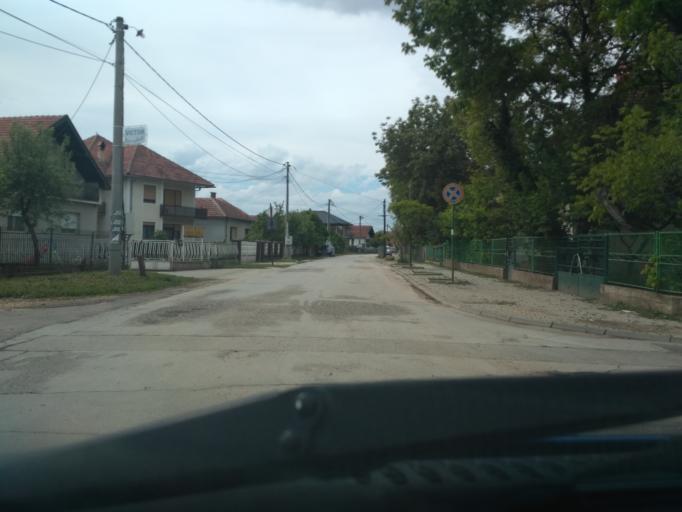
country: RS
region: Central Serbia
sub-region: Pomoravski Okrug
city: Svilajnac
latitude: 44.2264
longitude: 21.2062
